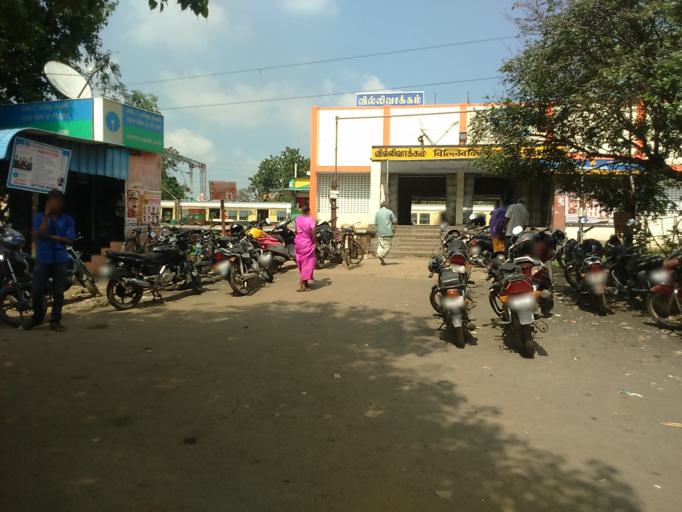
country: IN
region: Tamil Nadu
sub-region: Thiruvallur
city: Ambattur
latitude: 13.1098
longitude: 80.2088
